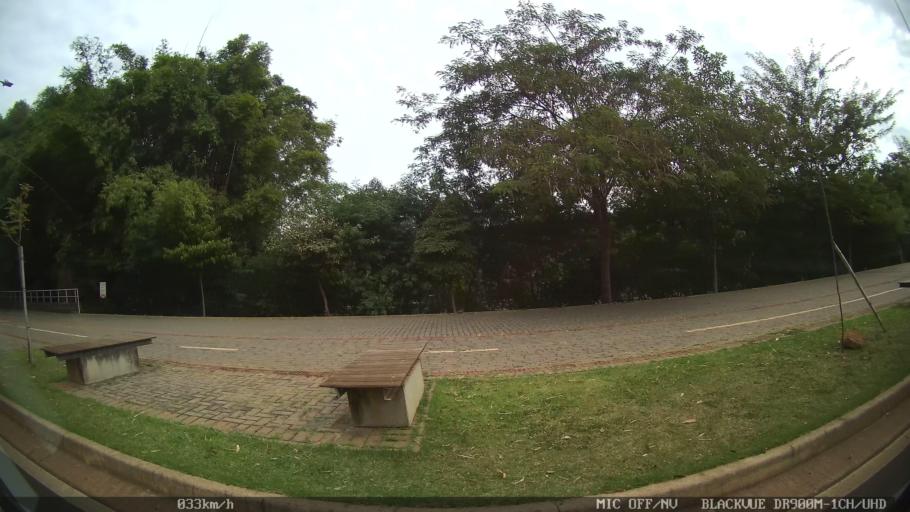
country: BR
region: Sao Paulo
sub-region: Piracicaba
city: Piracicaba
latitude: -22.7101
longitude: -47.6505
